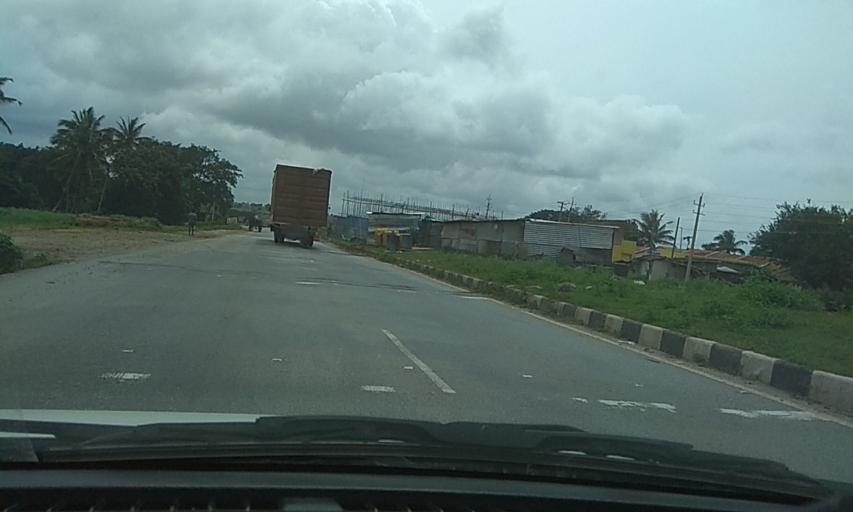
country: IN
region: Karnataka
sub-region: Davanagere
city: Mayakonda
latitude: 14.3665
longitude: 76.1570
